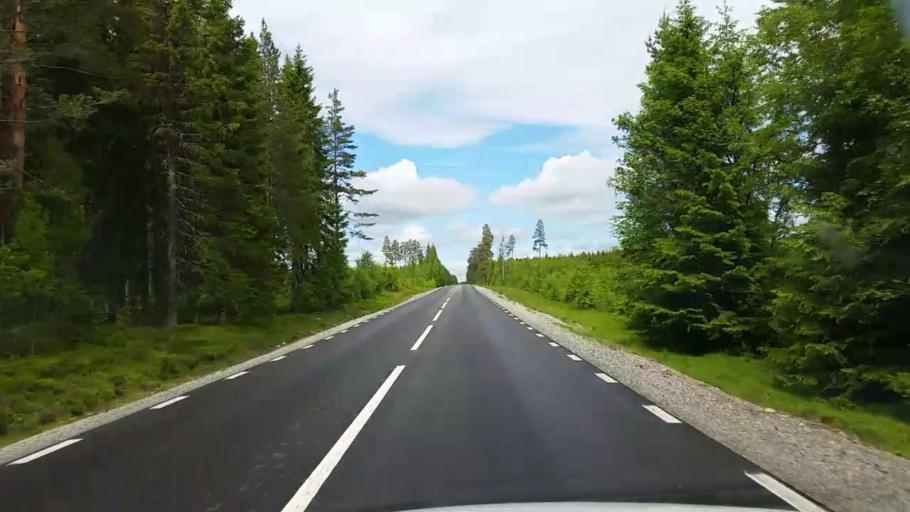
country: SE
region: Gaevleborg
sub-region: Sandvikens Kommun
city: Jarbo
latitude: 60.9038
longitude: 16.3775
